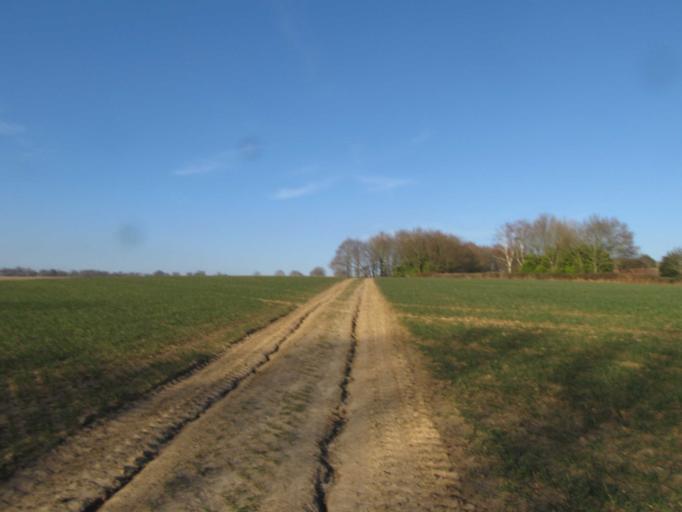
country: GB
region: England
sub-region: West Sussex
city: Petworth
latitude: 50.9769
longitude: -0.6318
